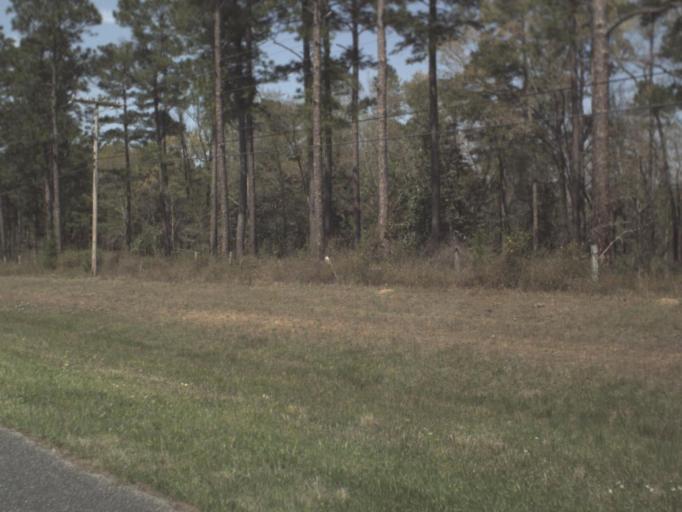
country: US
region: Florida
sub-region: Gadsden County
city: Midway
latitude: 30.5412
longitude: -84.4800
